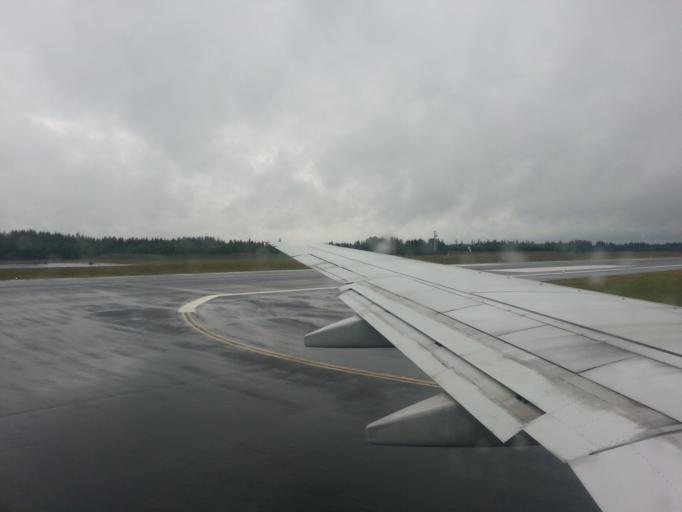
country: NO
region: Akershus
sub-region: Ullensaker
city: Jessheim
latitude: 60.1806
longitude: 11.1098
